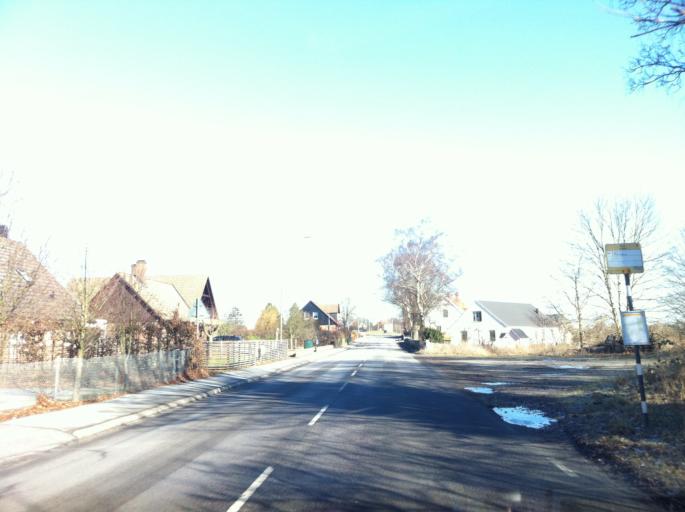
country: SE
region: Skane
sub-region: Svedala Kommun
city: Klagerup
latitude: 55.5733
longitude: 13.1984
